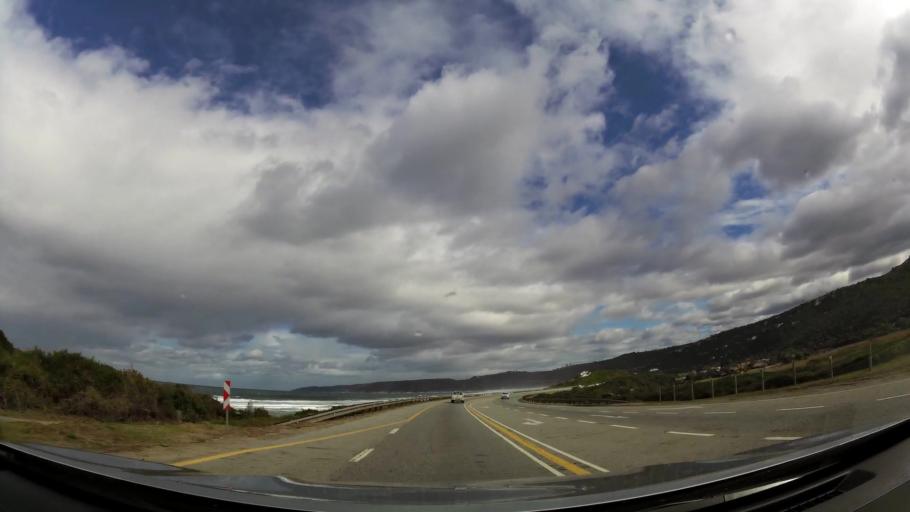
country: ZA
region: Western Cape
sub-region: Eden District Municipality
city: George
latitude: -33.9974
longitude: 22.6009
